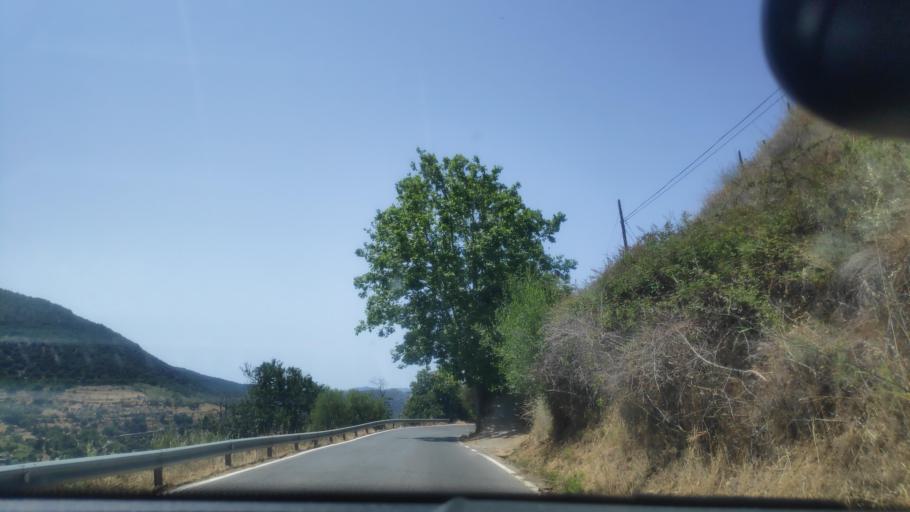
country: ES
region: Andalusia
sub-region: Provincia de Granada
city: Trevelez
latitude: 36.9900
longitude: -3.2707
